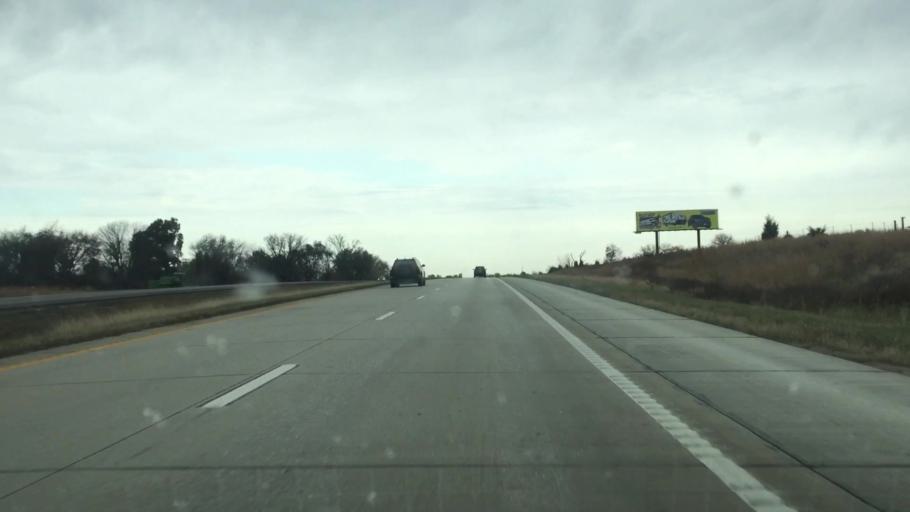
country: US
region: Missouri
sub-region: Saint Clair County
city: Osceola
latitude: 38.1665
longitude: -93.7220
